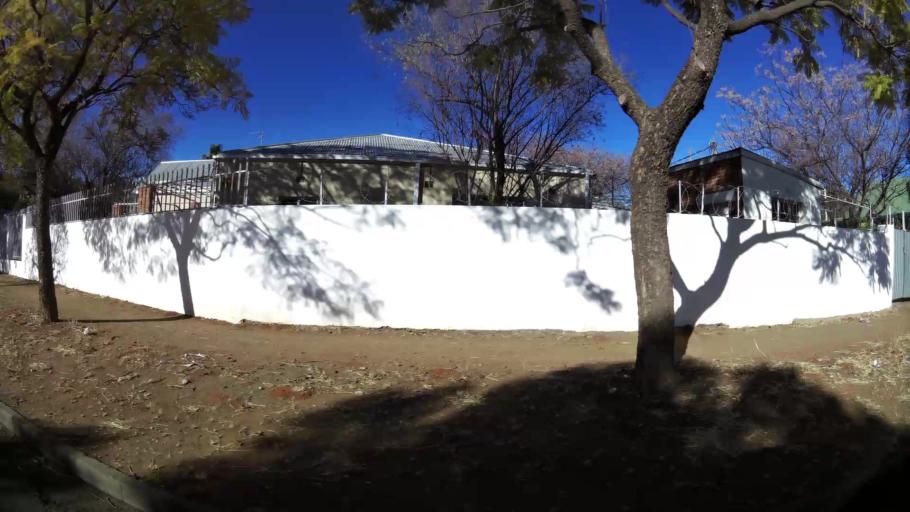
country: ZA
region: Northern Cape
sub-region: Frances Baard District Municipality
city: Kimberley
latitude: -28.7422
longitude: 24.7769
